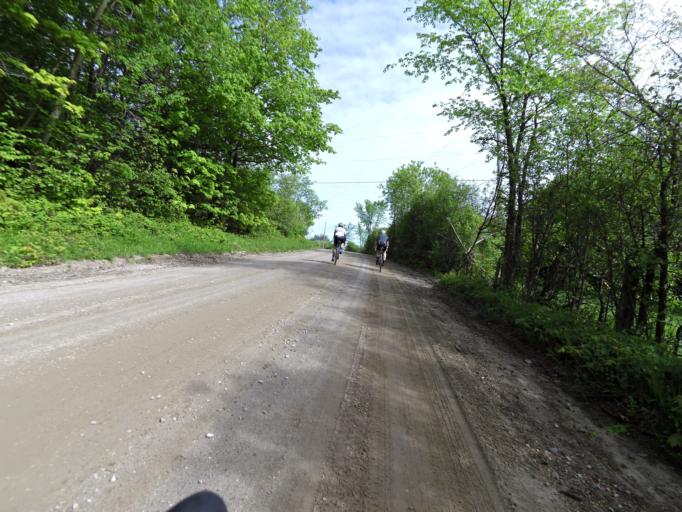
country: CA
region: Quebec
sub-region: Outaouais
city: Wakefield
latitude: 45.7020
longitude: -75.8963
